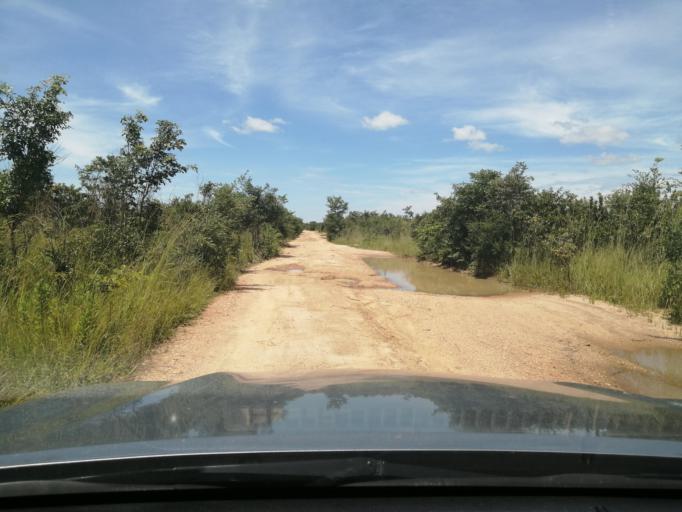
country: ZM
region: Central
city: Chibombo
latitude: -15.0381
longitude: 27.8255
